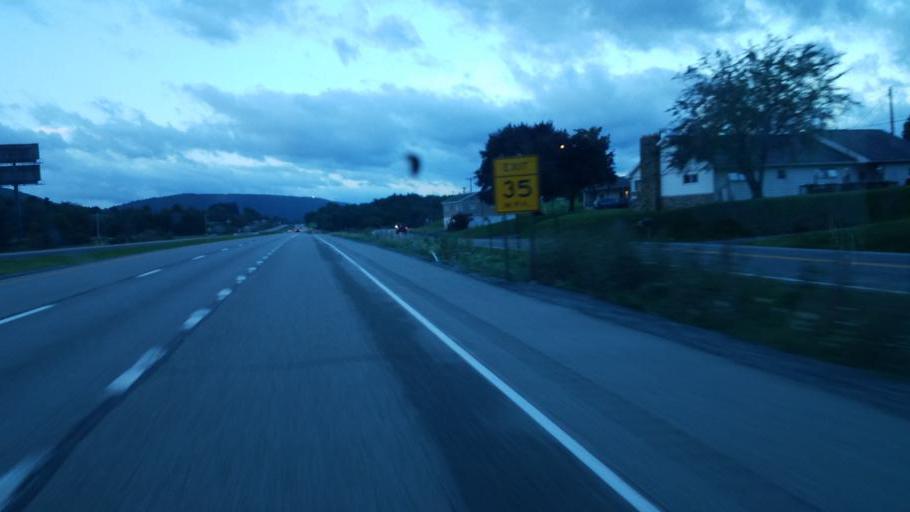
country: US
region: Pennsylvania
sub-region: Bedford County
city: Earlston
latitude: 39.9826
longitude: -78.2443
